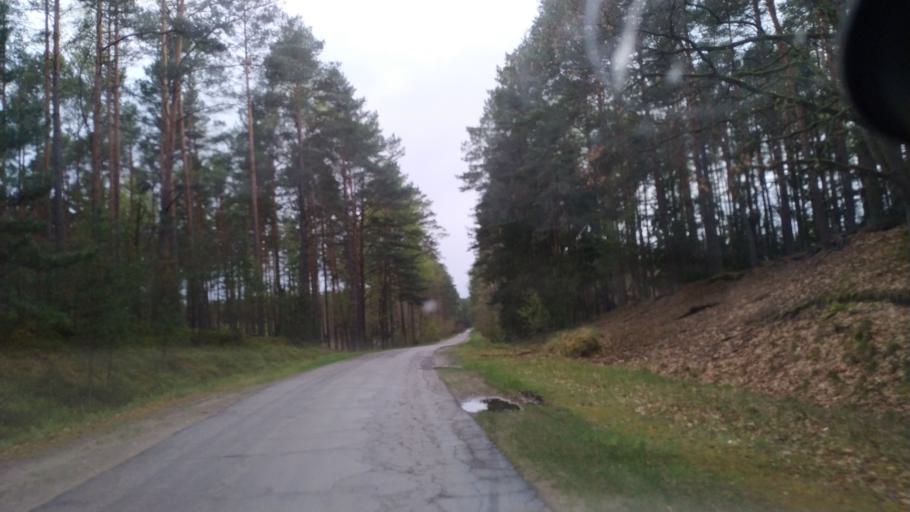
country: PL
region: Pomeranian Voivodeship
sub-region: Powiat starogardzki
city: Osiek
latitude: 53.6845
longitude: 18.5075
